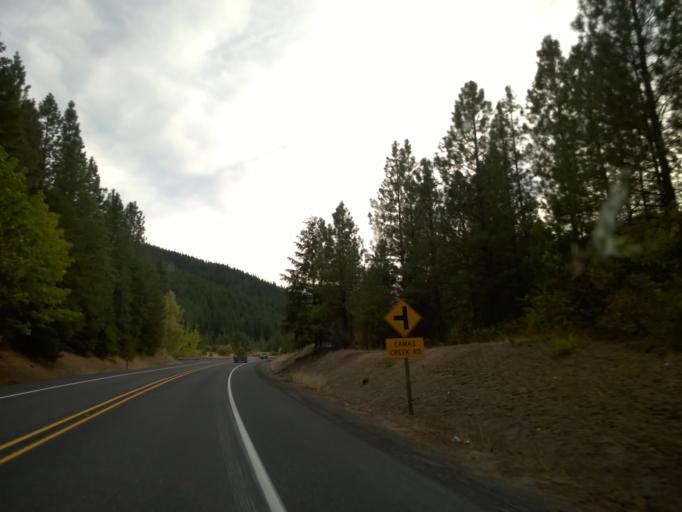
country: US
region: Washington
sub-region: Chelan County
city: Leavenworth
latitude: 47.4943
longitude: -120.6337
